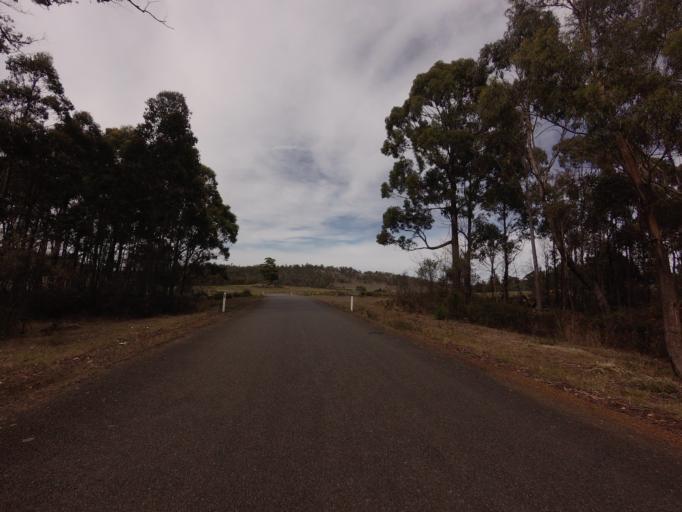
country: AU
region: Tasmania
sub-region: Sorell
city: Sorell
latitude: -42.5251
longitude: 147.6510
